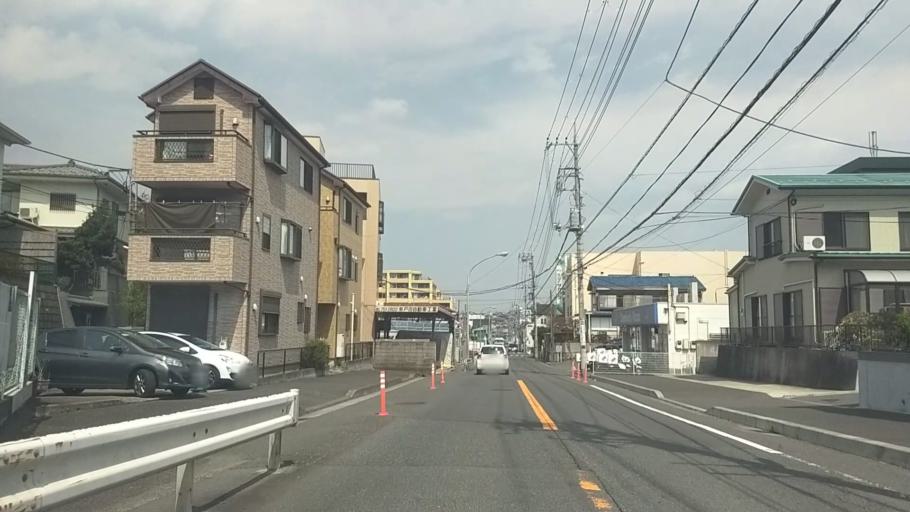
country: JP
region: Kanagawa
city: Yokohama
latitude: 35.4096
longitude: 139.6107
